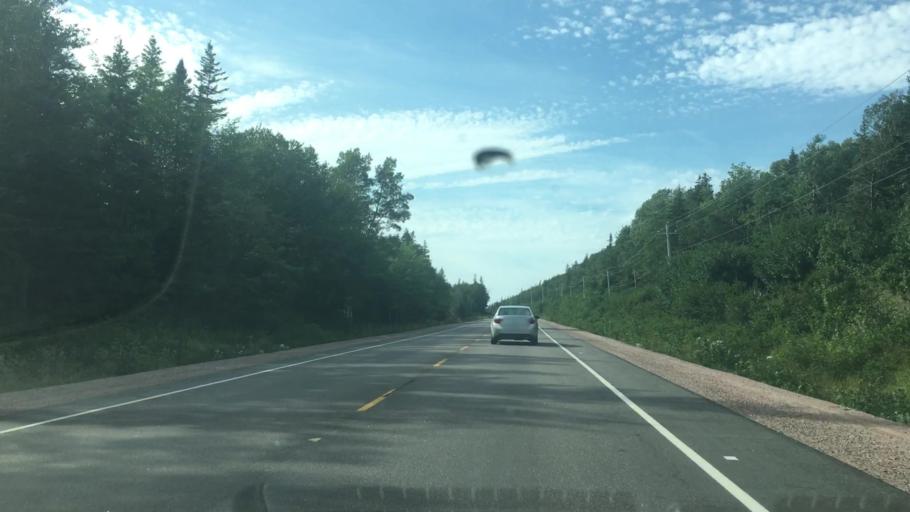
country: CA
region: Nova Scotia
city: Sydney Mines
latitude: 46.8159
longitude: -60.3432
